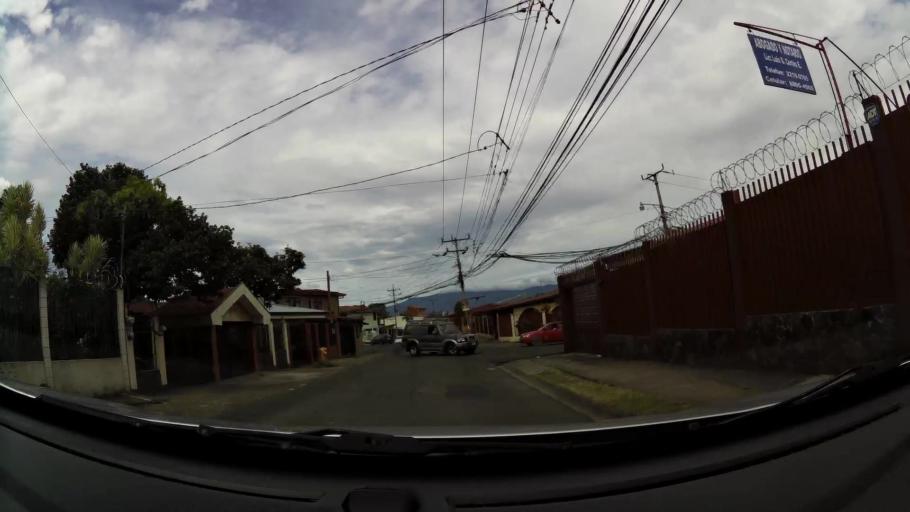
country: CR
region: San Jose
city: San Rafael Arriba
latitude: 9.8937
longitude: -84.0727
